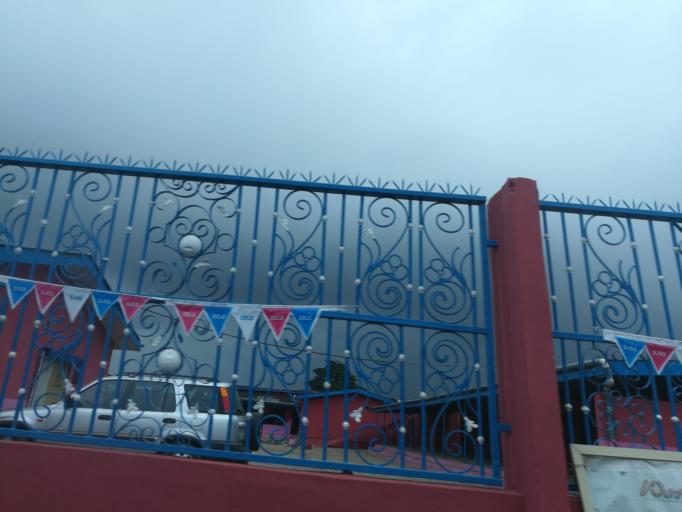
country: NG
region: Lagos
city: Agege
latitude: 6.6097
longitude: 3.3294
